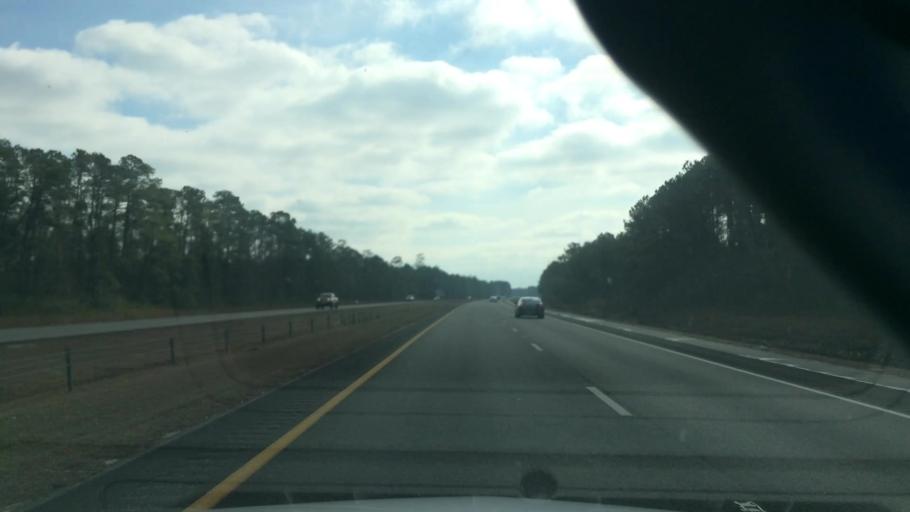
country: US
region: North Carolina
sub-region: Pender County
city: Burgaw
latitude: 34.5490
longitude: -77.8942
